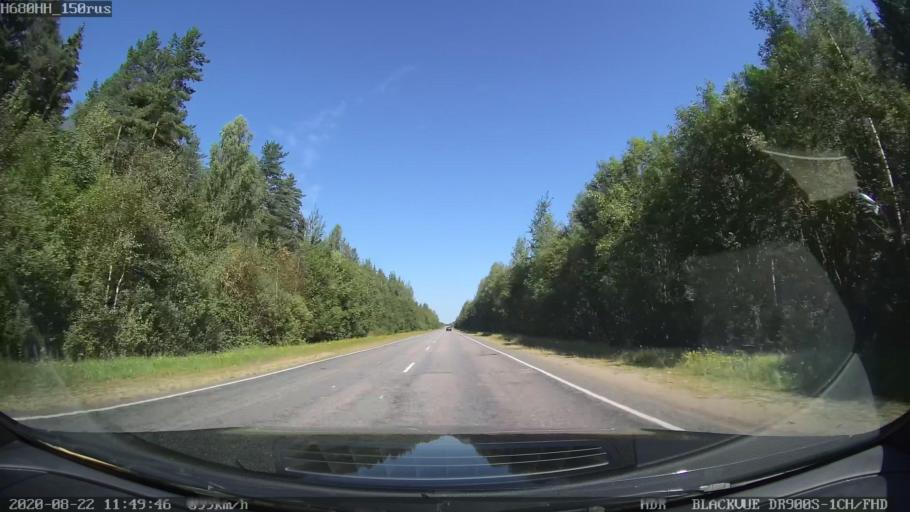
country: RU
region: Tverskaya
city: Sakharovo
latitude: 57.0803
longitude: 36.1130
